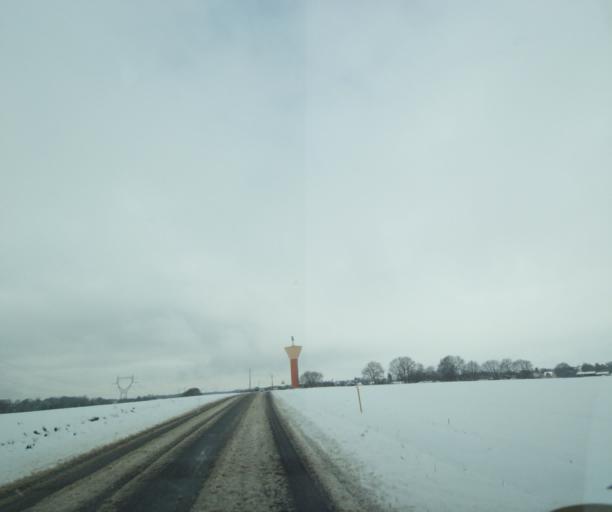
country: FR
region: Champagne-Ardenne
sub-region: Departement de la Haute-Marne
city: Montier-en-Der
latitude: 48.5091
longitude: 4.7092
